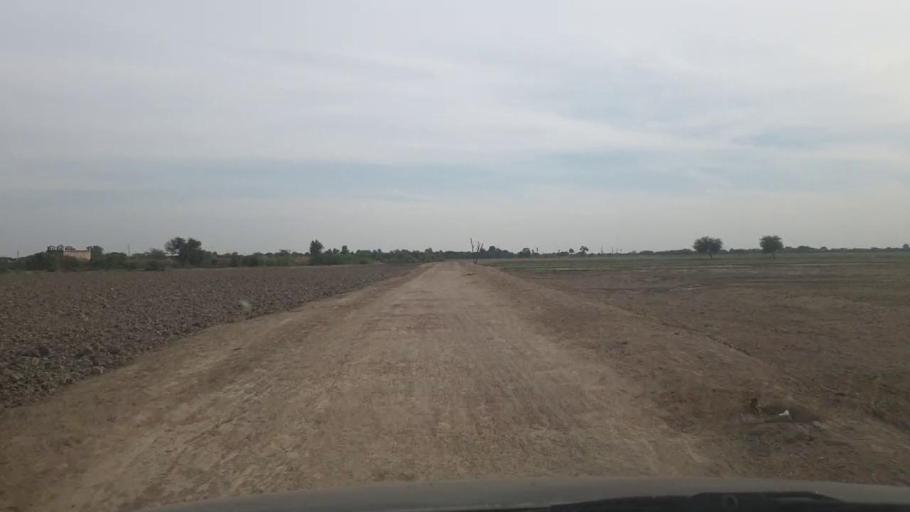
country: PK
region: Sindh
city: Kunri
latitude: 25.2803
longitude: 69.5999
